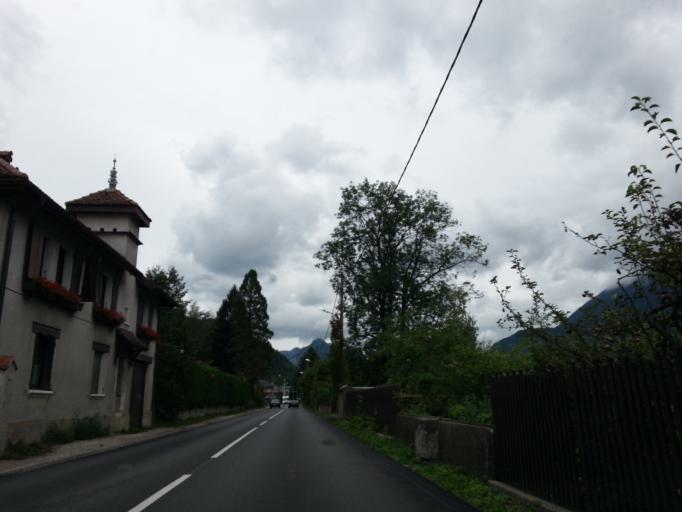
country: FR
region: Rhone-Alpes
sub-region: Departement de la Haute-Savoie
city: Talloires
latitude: 45.8111
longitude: 6.2104
